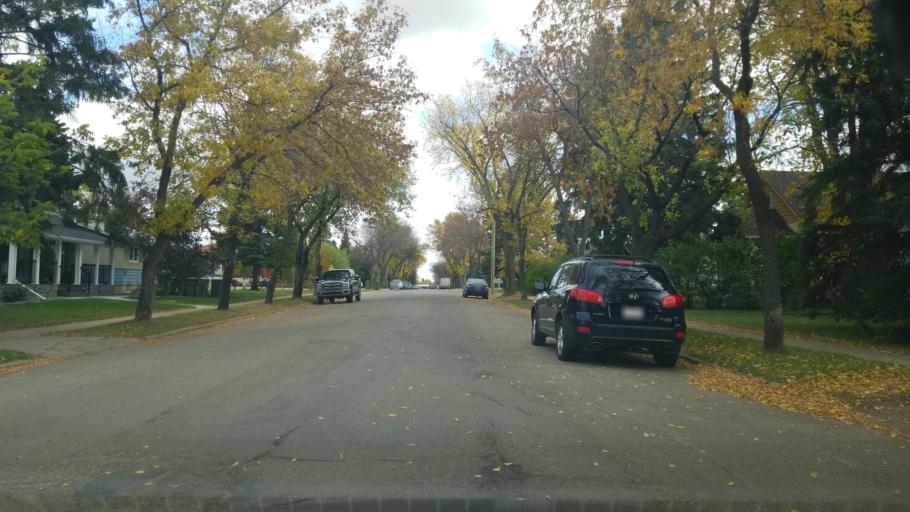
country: CA
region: Saskatchewan
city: Lloydminster
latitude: 53.2807
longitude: -110.0141
